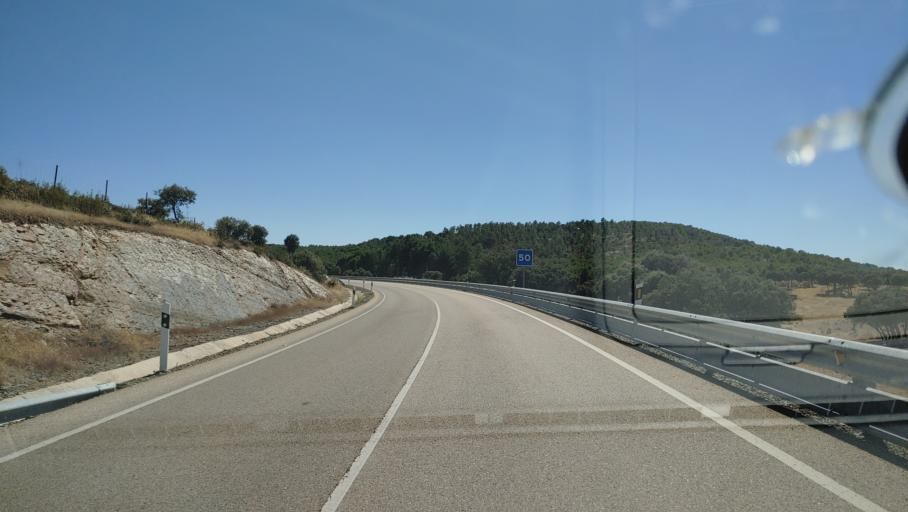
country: ES
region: Andalusia
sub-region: Provincia de Jaen
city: Genave
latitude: 38.4908
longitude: -2.7672
